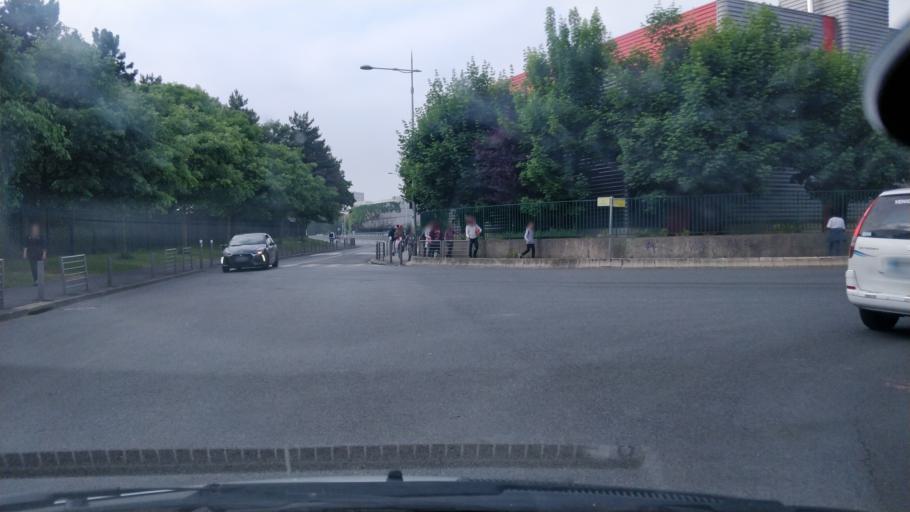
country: FR
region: Ile-de-France
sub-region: Departement de Seine-Saint-Denis
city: Bagnolet
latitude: 48.8654
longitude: 2.4254
